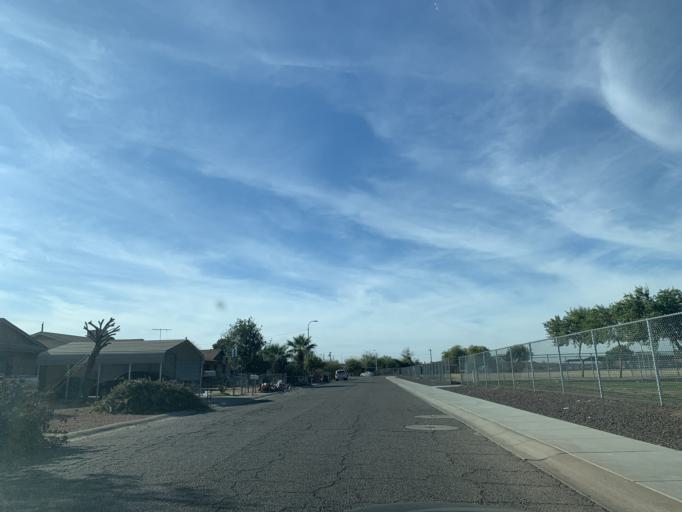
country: US
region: Arizona
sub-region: Maricopa County
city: Laveen
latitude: 33.3981
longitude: -112.1397
